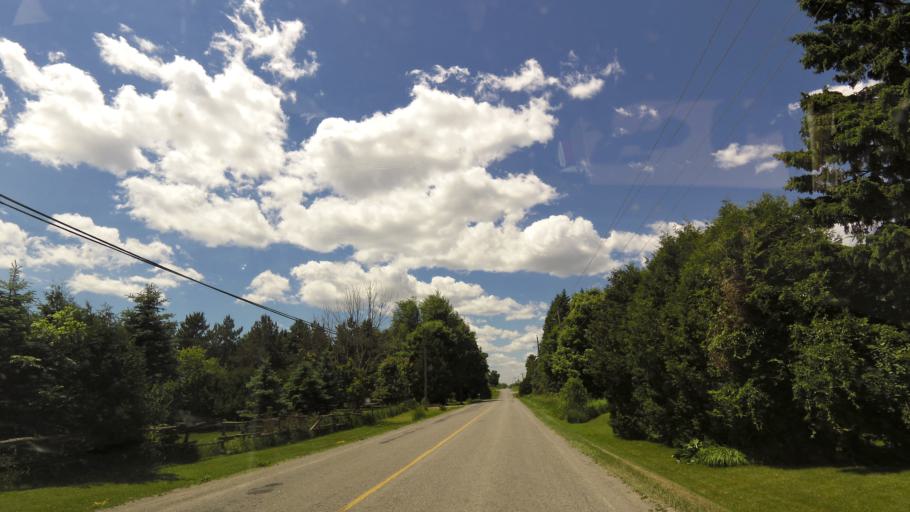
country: CA
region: Ontario
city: Omemee
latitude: 43.9731
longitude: -78.5135
